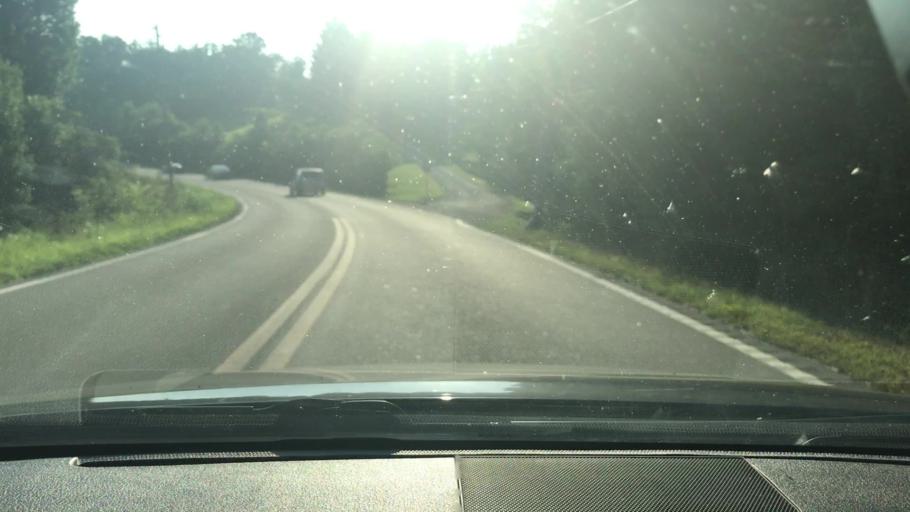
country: US
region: Tennessee
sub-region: Cheatham County
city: Ashland City
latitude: 36.2799
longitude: -87.1116
